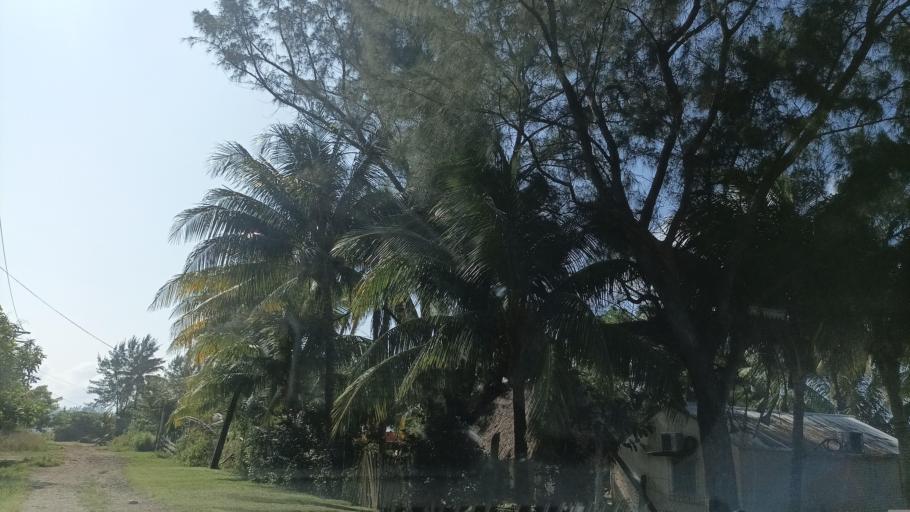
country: MX
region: Veracruz
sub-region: Coatzacoalcos
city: Fraccionamiento Ciudad Olmeca
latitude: 18.2081
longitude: -94.6099
